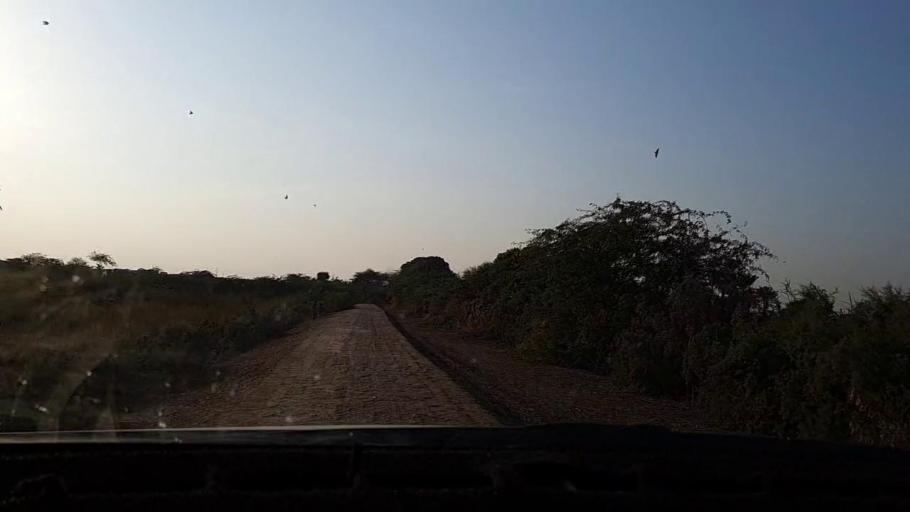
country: PK
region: Sindh
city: Tando Mittha Khan
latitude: 25.8692
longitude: 69.2729
